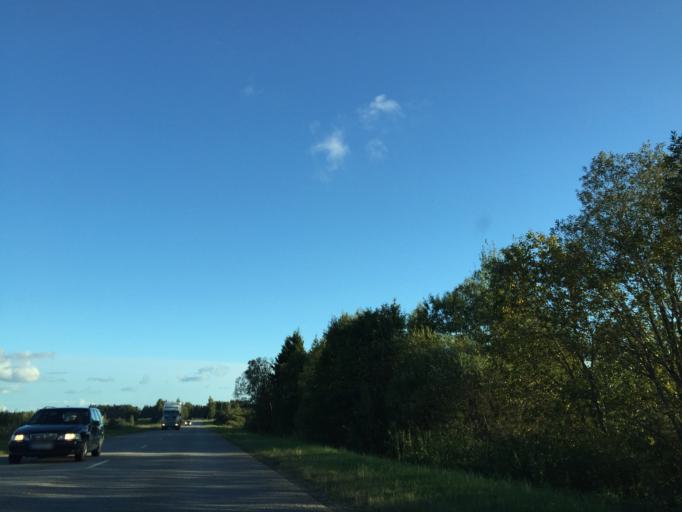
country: LV
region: Kuldigas Rajons
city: Kuldiga
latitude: 56.9228
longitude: 22.0527
